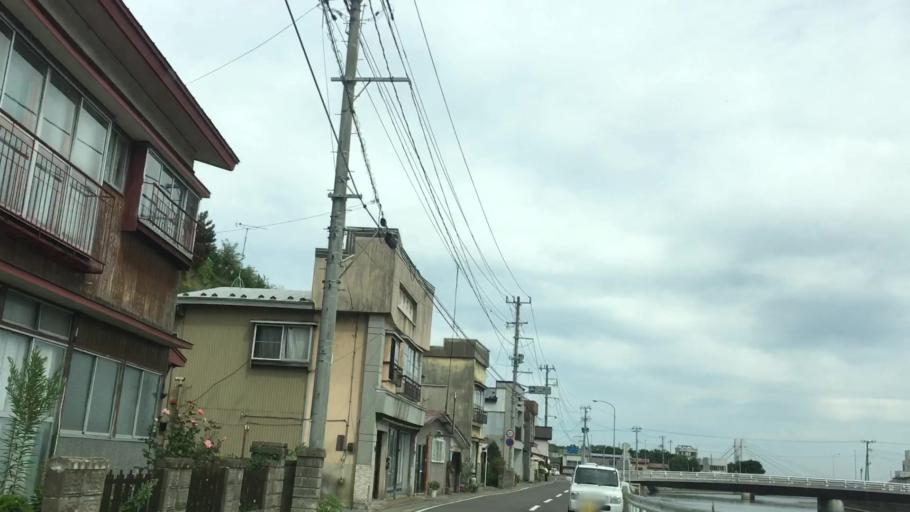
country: JP
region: Aomori
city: Shimokizukuri
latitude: 40.7760
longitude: 140.2166
